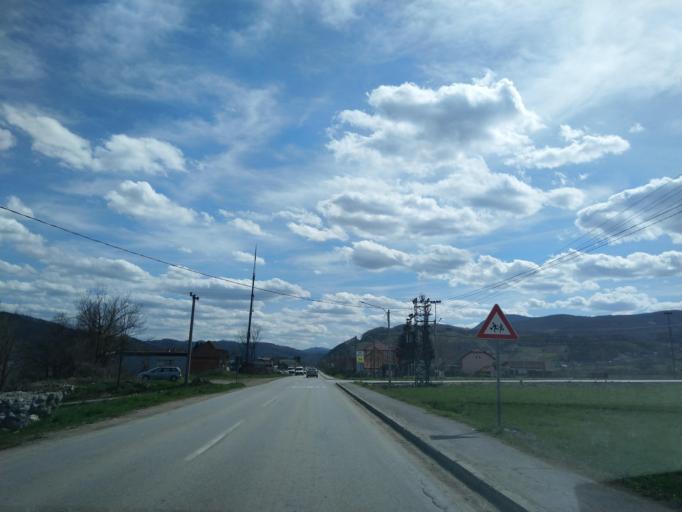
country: RS
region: Central Serbia
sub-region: Zlatiborski Okrug
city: Arilje
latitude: 43.7133
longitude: 20.1161
